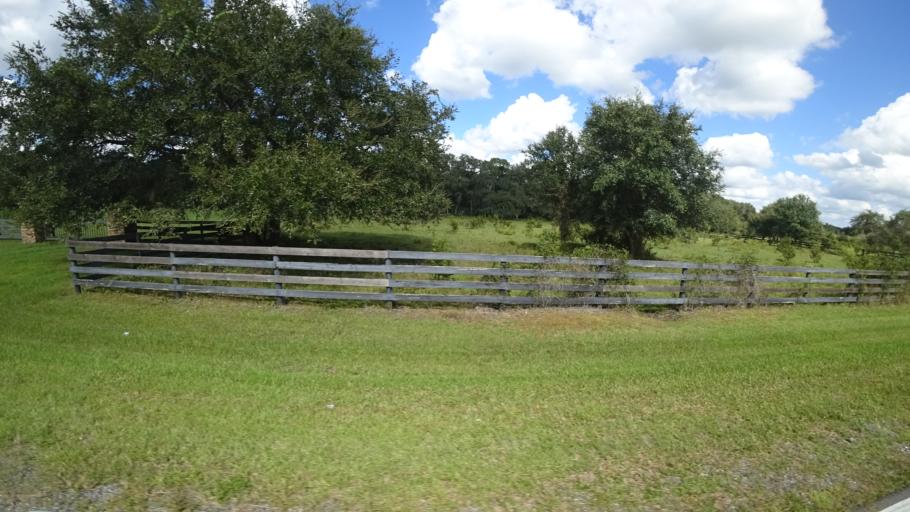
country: US
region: Florida
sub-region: Sarasota County
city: Lake Sarasota
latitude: 27.2889
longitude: -82.2264
